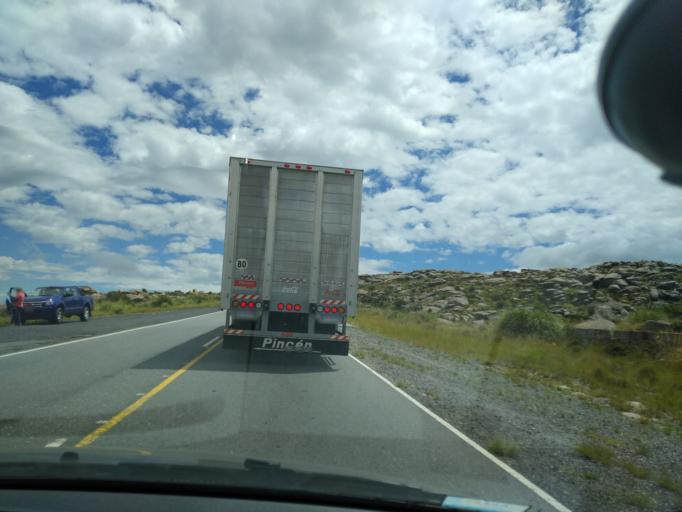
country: AR
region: Cordoba
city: Villa Cura Brochero
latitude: -31.6197
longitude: -64.9110
